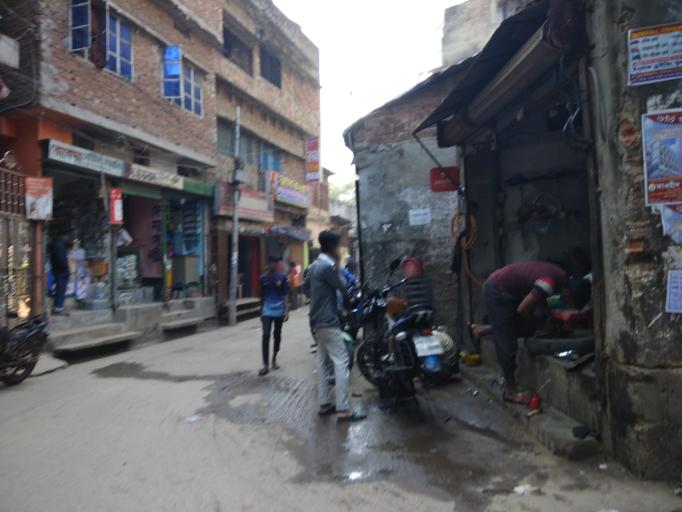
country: BD
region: Dhaka
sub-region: Dhaka
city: Dhaka
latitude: 23.7183
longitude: 90.4062
